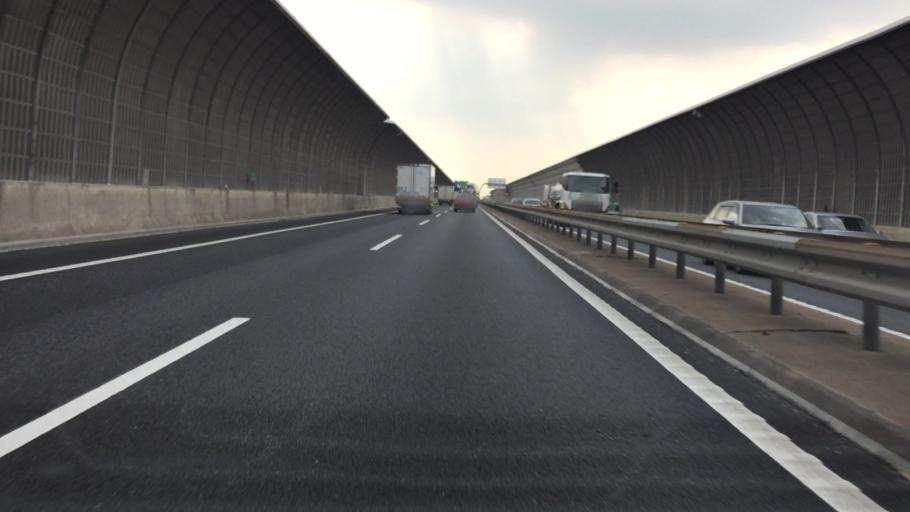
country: JP
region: Saitama
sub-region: Kawaguchi-shi
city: Hatogaya-honcho
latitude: 35.8506
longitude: 139.7577
